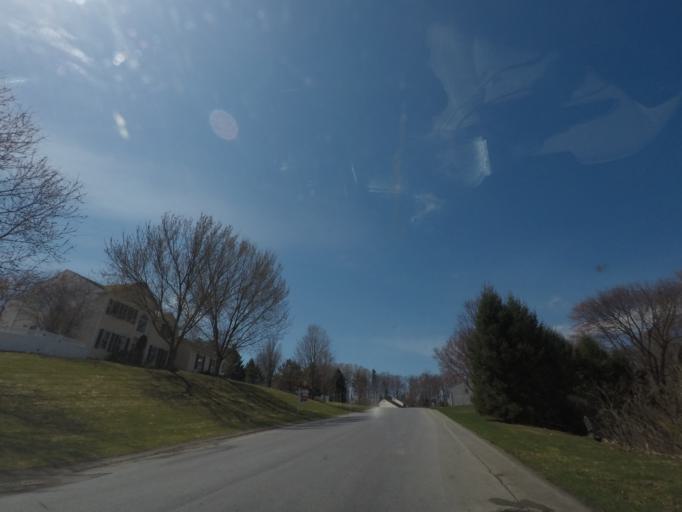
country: US
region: New York
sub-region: Rensselaer County
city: Wynantskill
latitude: 42.6944
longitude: -73.6612
